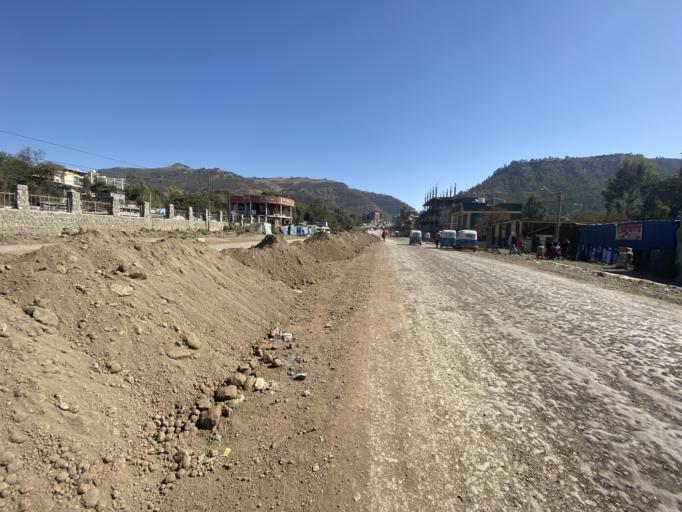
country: ET
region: Amhara
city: Robit
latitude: 11.8280
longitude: 39.5966
